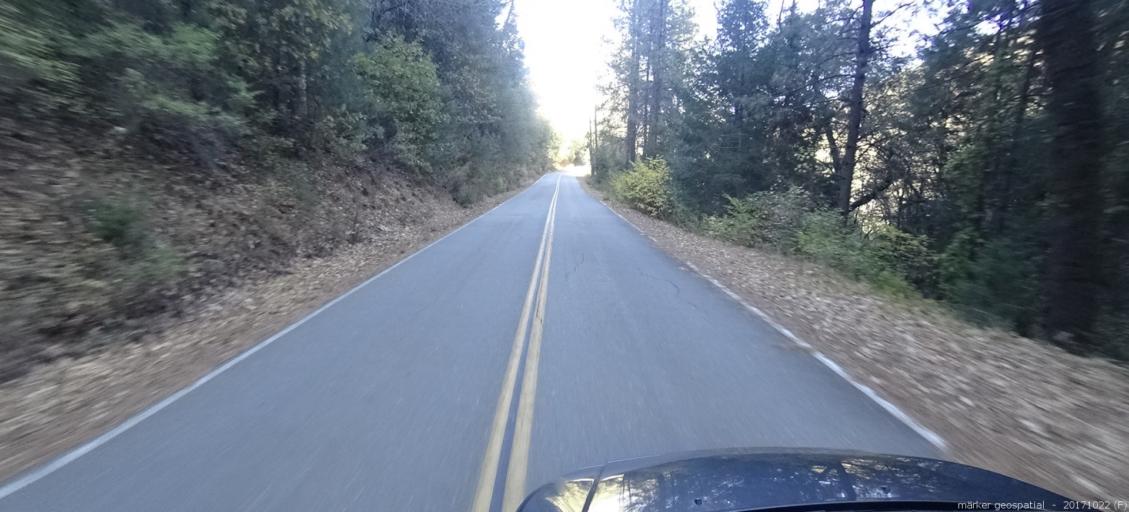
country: US
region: California
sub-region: Shasta County
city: Bella Vista
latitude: 40.8988
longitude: -122.2301
